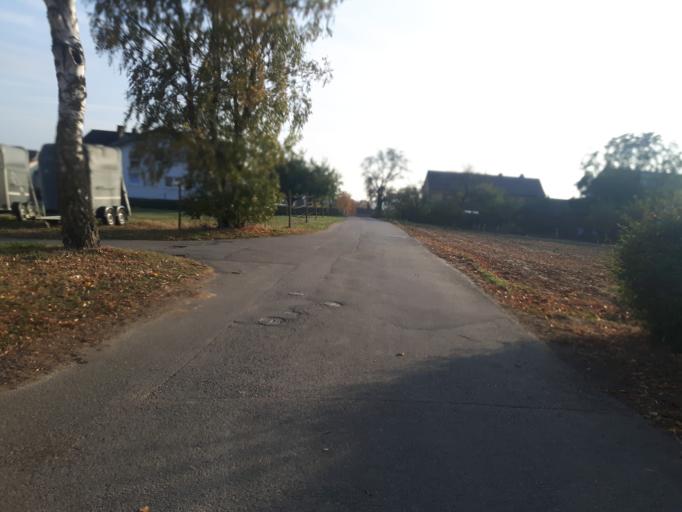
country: DE
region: Baden-Wuerttemberg
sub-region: Regierungsbezirk Stuttgart
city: Untereisesheim
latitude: 49.1666
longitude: 9.1721
